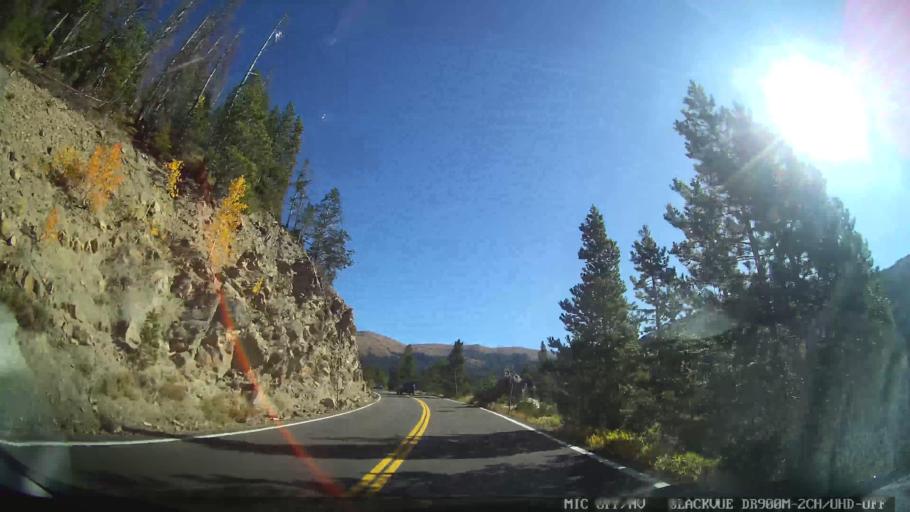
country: US
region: Colorado
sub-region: Larimer County
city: Estes Park
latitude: 40.3987
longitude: -105.8317
